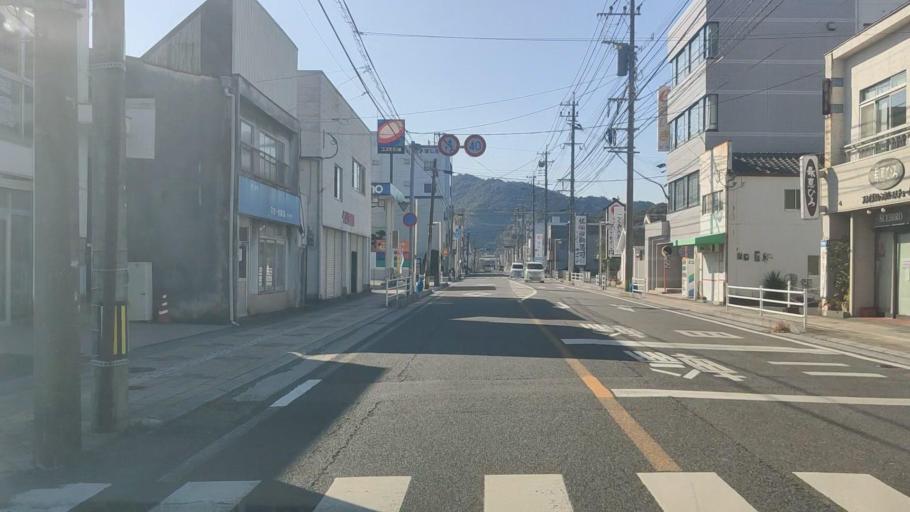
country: JP
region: Oita
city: Saiki
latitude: 32.9594
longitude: 131.8970
